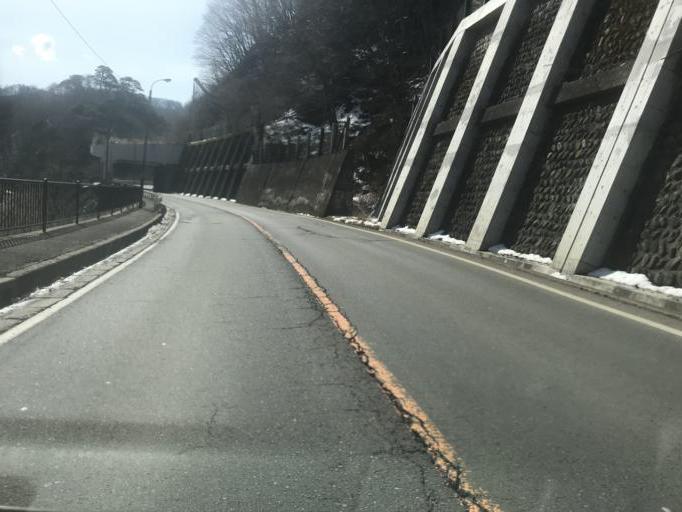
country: JP
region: Nagano
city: Saku
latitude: 36.0116
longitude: 138.4922
